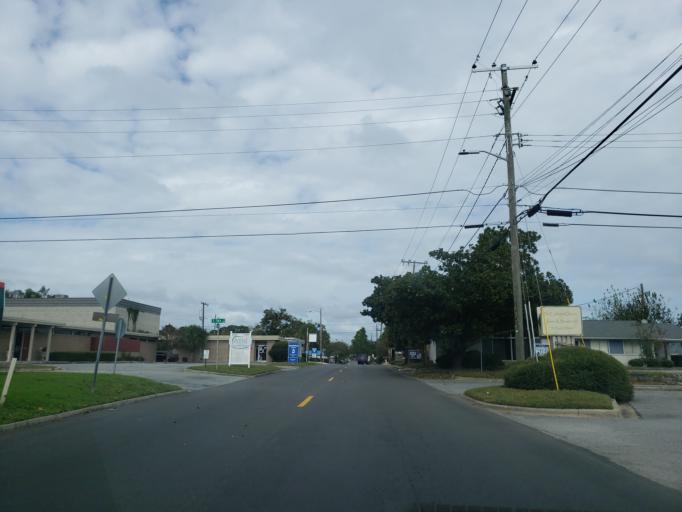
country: US
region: Georgia
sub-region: Chatham County
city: Thunderbolt
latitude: 32.0273
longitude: -81.0972
